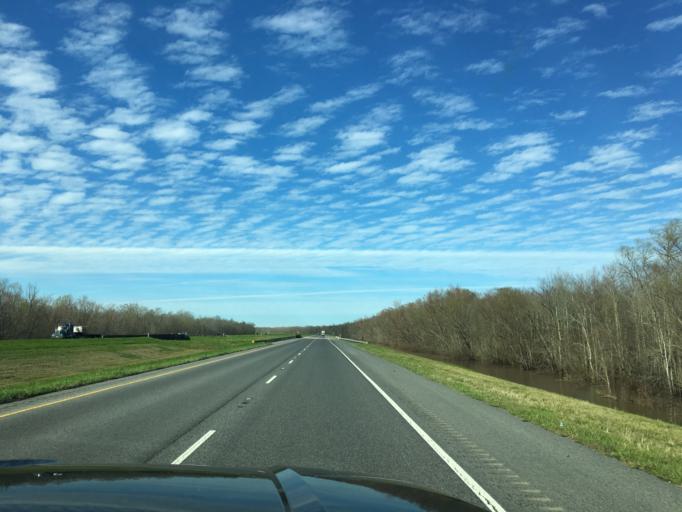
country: US
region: Louisiana
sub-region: Saint Landry Parish
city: Opelousas
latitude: 30.6836
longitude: -92.0770
